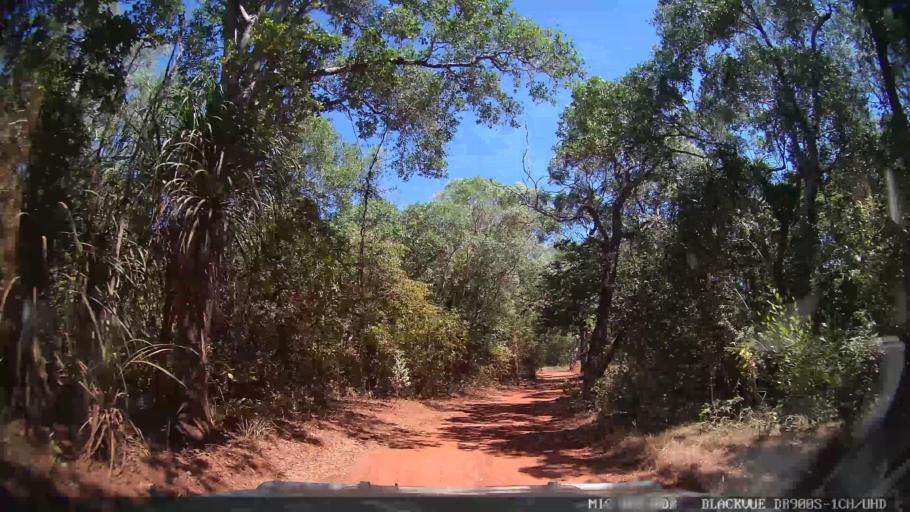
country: AU
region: Queensland
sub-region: Torres
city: Thursday Island
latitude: -10.7078
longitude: 142.5291
